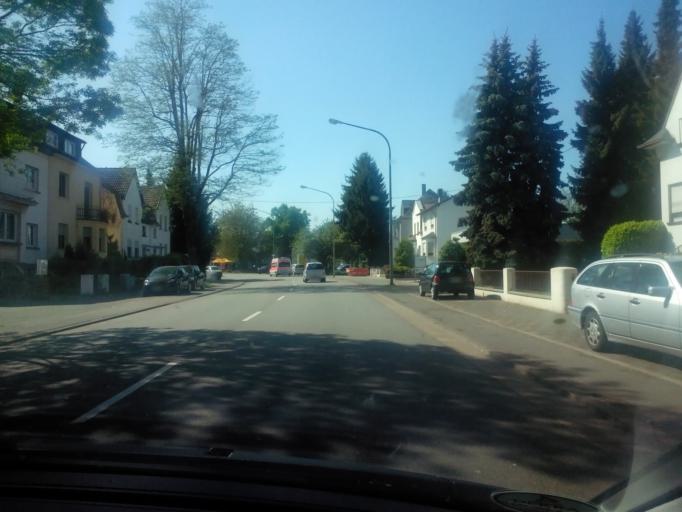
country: DE
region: Saarland
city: Saarlouis
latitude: 49.3271
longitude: 6.7448
